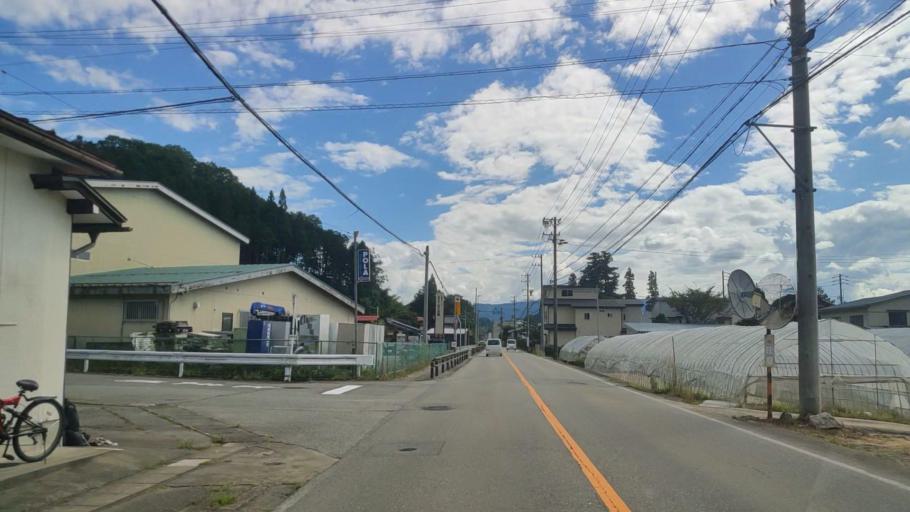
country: JP
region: Gifu
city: Takayama
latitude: 36.1667
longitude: 137.2486
